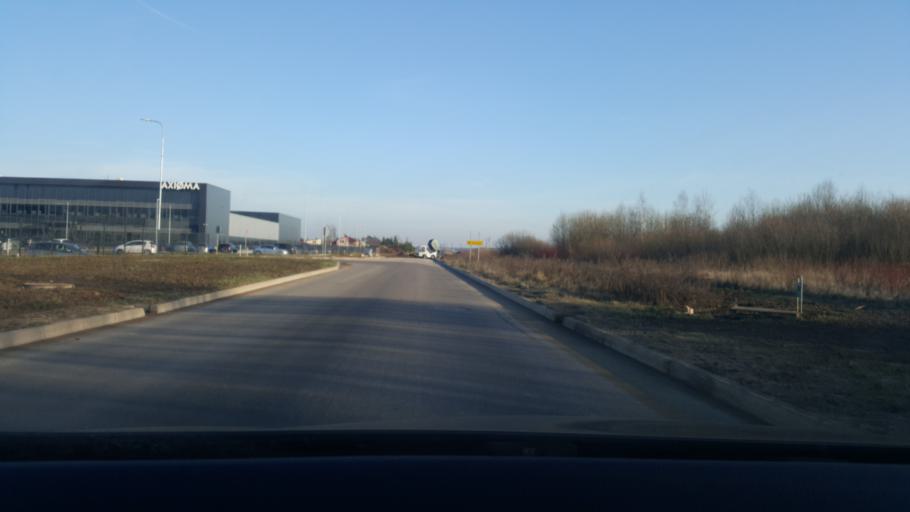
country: LT
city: Ramuciai
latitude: 54.9388
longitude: 24.0160
